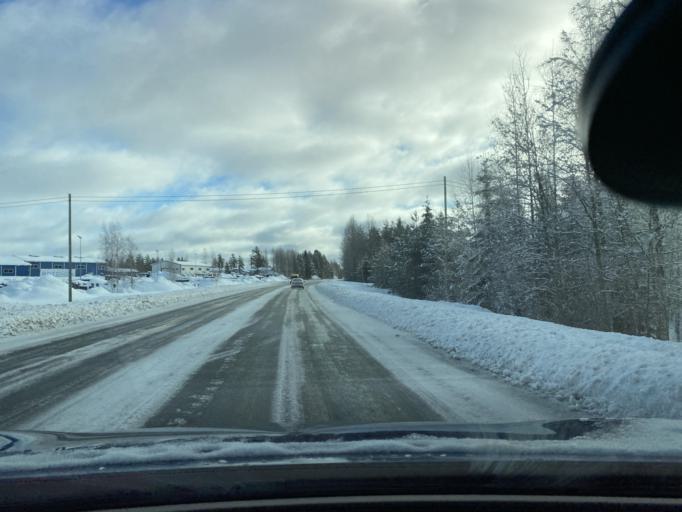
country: FI
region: Southern Savonia
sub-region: Mikkeli
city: Kangasniemi
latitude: 62.0107
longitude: 26.6349
